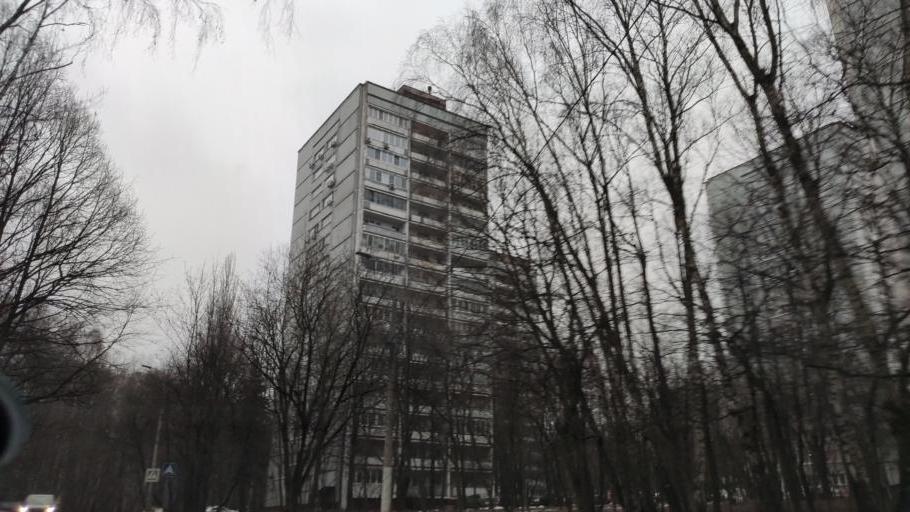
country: RU
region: Moscow
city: Troparevo
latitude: 55.6599
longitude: 37.4901
